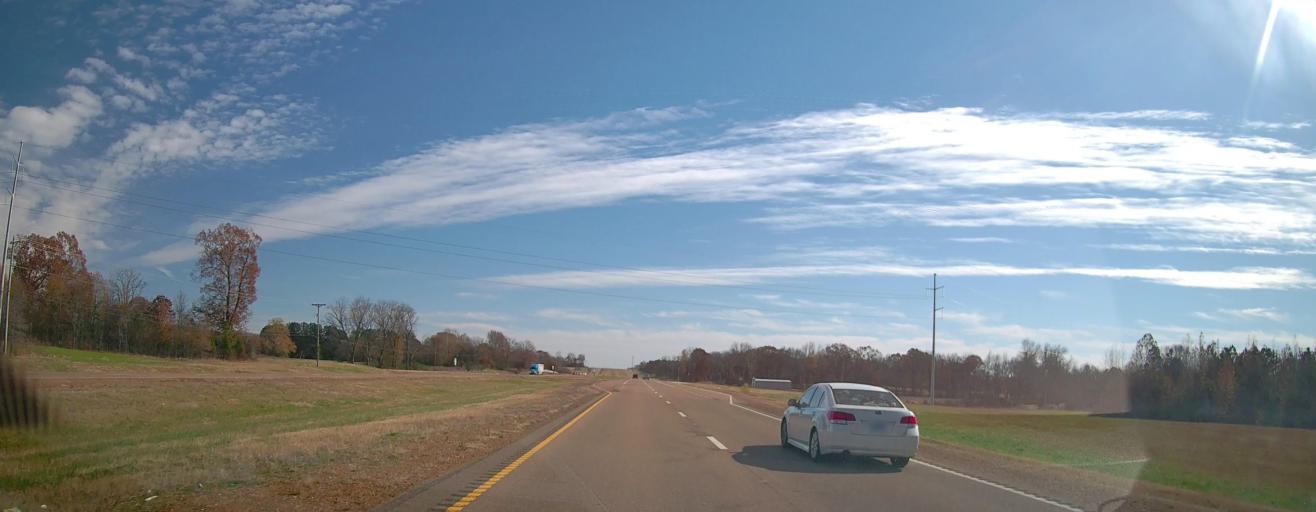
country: US
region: Tennessee
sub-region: Fayette County
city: Piperton
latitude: 34.9743
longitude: -89.5664
